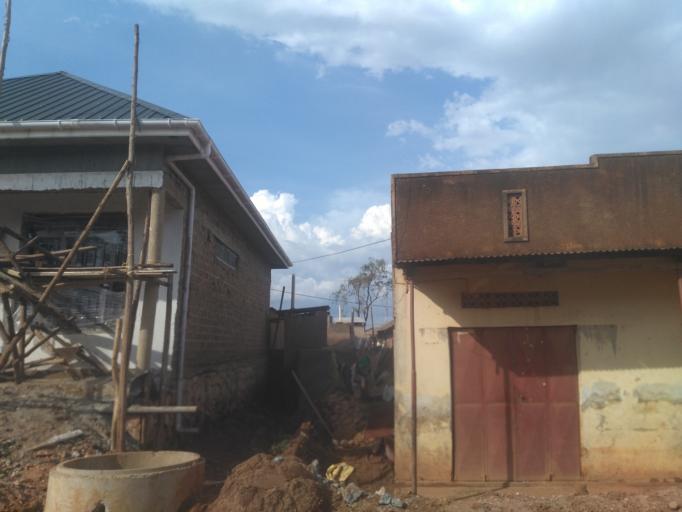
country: UG
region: Central Region
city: Kampala Central Division
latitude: 0.3618
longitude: 32.5724
